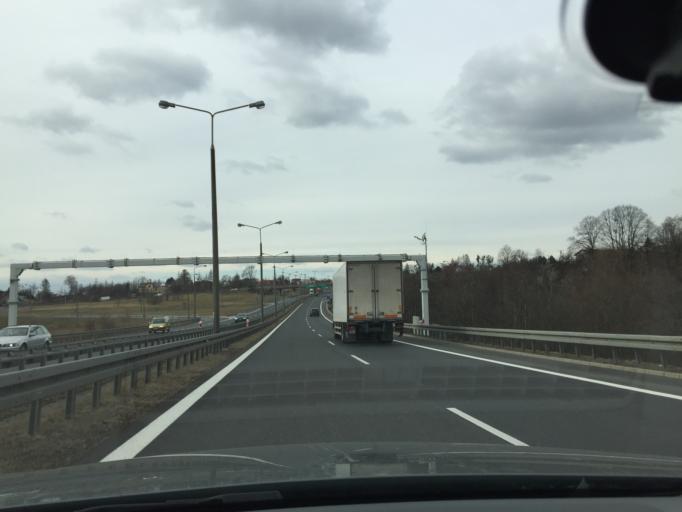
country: PL
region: Silesian Voivodeship
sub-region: Powiat cieszynski
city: Cieszyn
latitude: 49.7662
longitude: 18.6426
